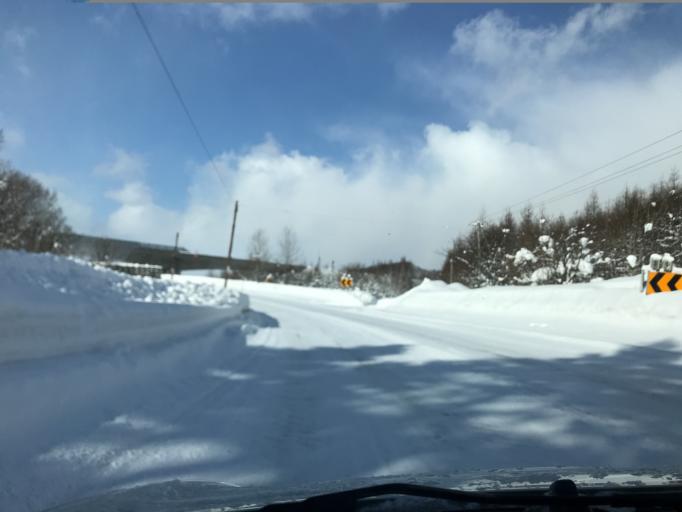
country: JP
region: Hokkaido
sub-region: Asahikawa-shi
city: Asahikawa
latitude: 43.9327
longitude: 142.4716
